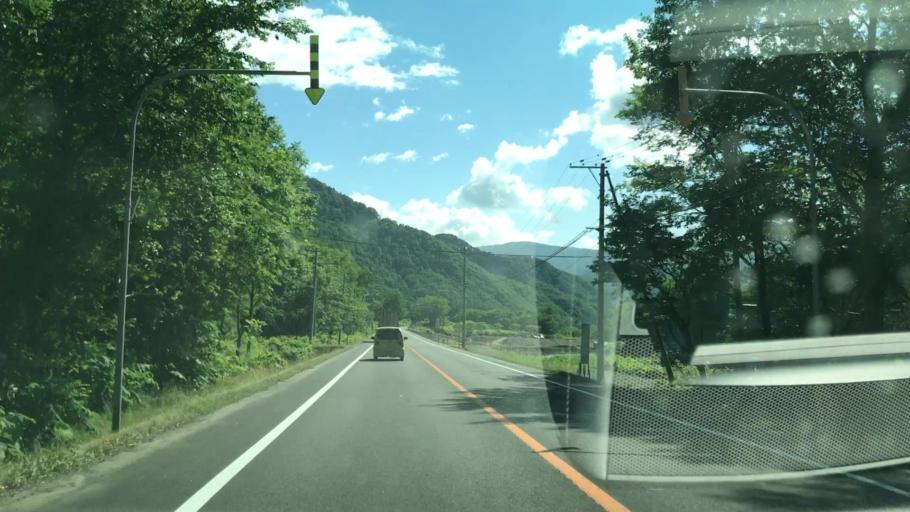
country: JP
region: Hokkaido
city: Shimo-furano
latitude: 42.9038
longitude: 142.5668
